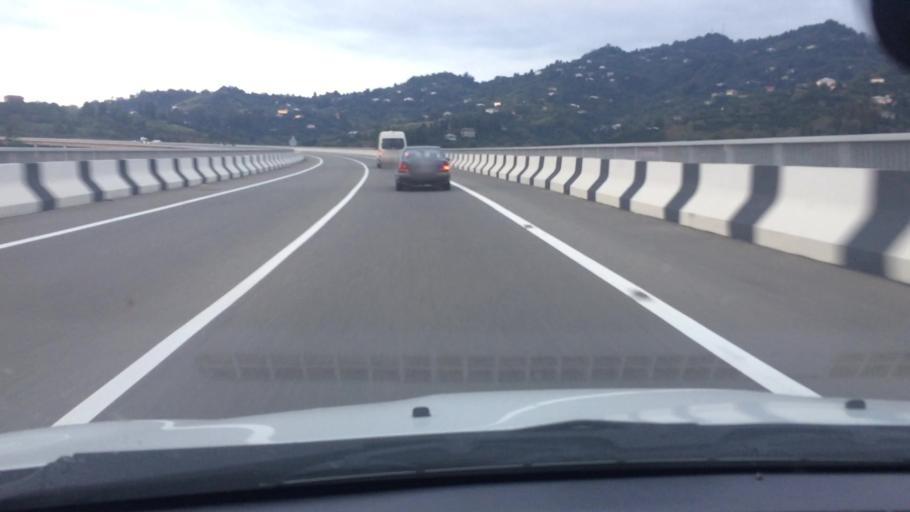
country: GE
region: Ajaria
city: Makhinjauri
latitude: 41.7114
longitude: 41.7500
